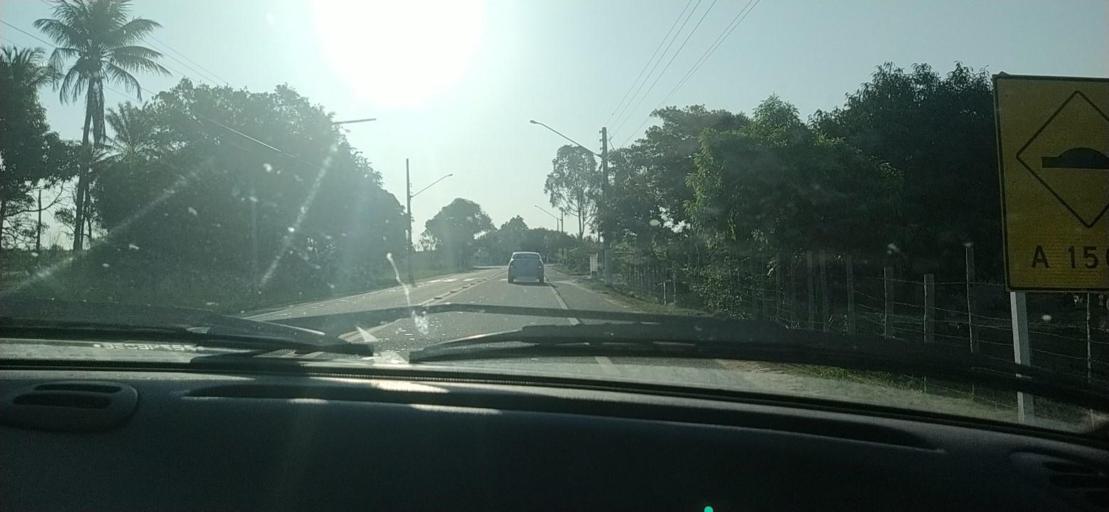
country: BR
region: Espirito Santo
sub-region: Conceicao Da Barra
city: Conceicao da Barra
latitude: -18.5660
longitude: -39.7620
